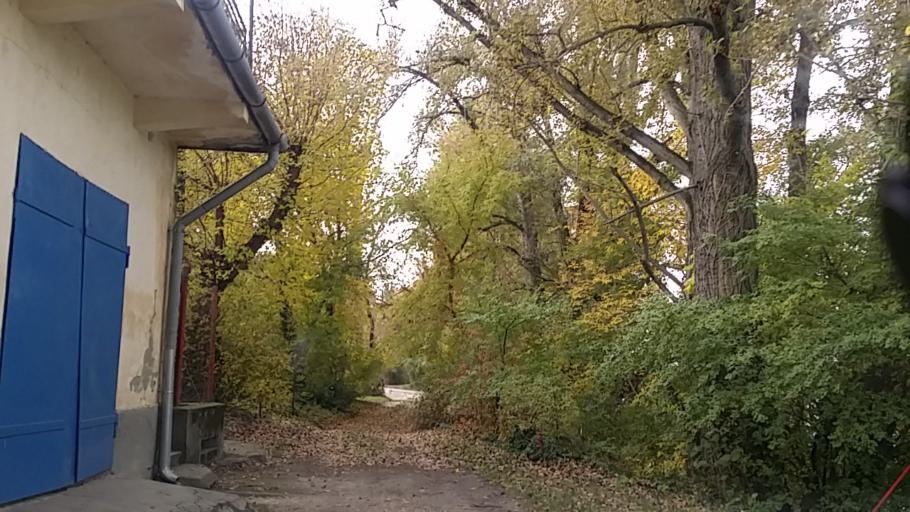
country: HU
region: Budapest
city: Budapest IV. keruelet
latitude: 47.5903
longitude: 19.0789
